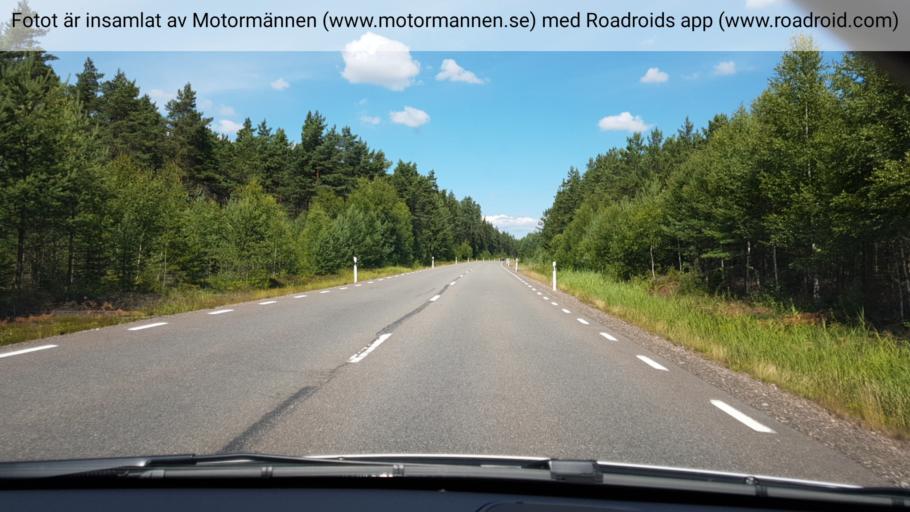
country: SE
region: Vaestra Goetaland
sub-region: Tibro Kommun
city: Tibro
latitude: 58.5307
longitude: 14.1498
